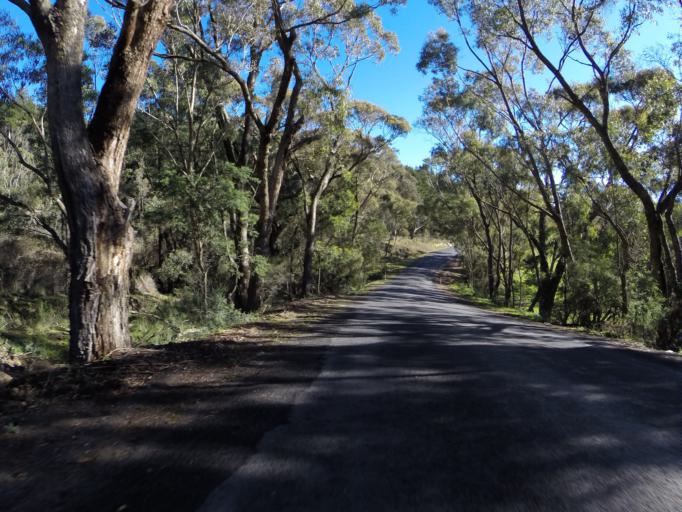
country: AU
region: New South Wales
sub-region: Oberon
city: Oberon
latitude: -33.6105
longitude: 149.8483
